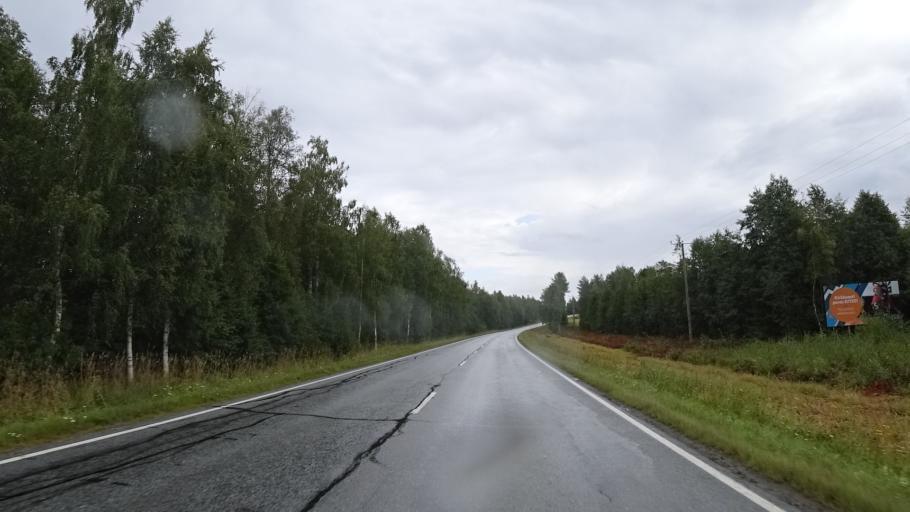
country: FI
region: North Karelia
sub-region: Keski-Karjala
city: Raeaekkylae
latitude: 62.0447
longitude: 29.5543
